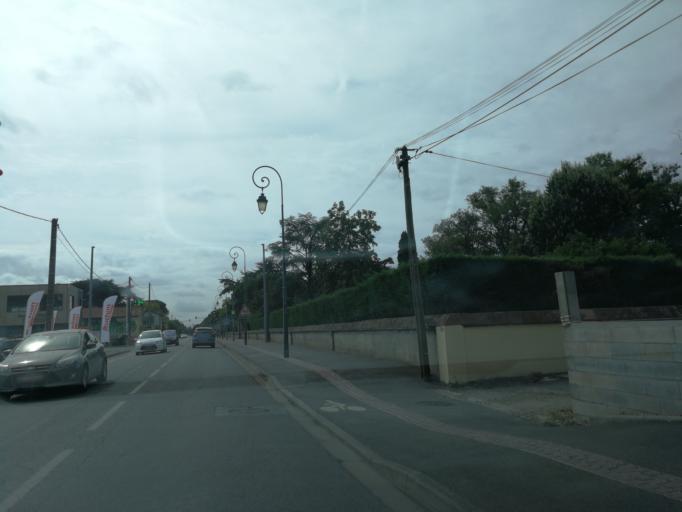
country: FR
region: Midi-Pyrenees
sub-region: Departement de la Haute-Garonne
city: Aucamville
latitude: 43.6768
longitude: 1.4239
